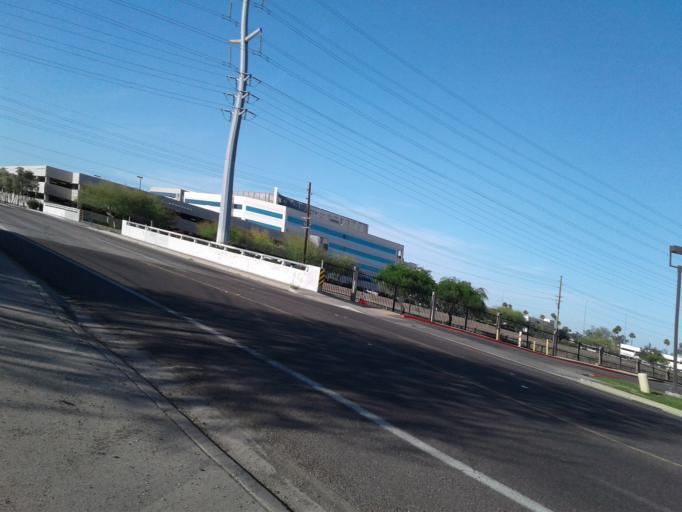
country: US
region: Arizona
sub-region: Maricopa County
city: Glendale
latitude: 33.5722
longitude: -112.1121
